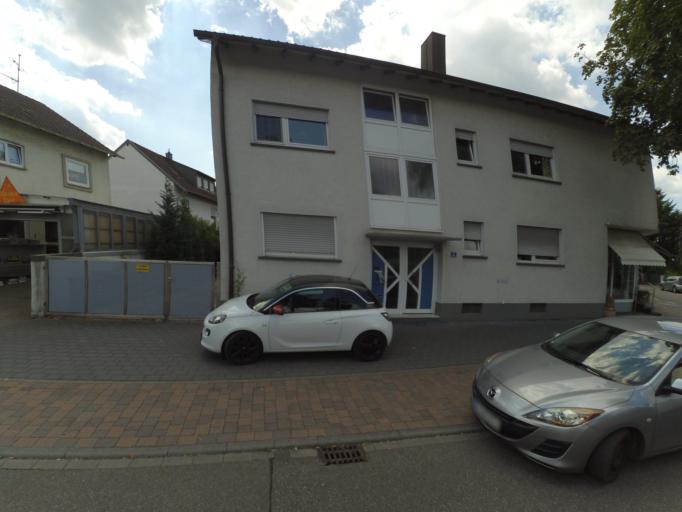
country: DE
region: Baden-Wuerttemberg
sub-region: Karlsruhe Region
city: Eggenstein-Leopoldshafen
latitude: 49.0804
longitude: 8.3921
